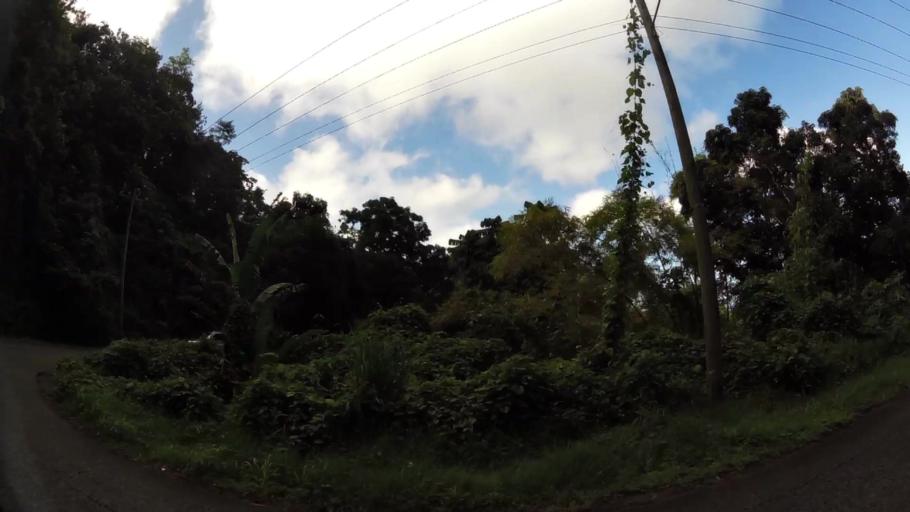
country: LC
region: Anse-la-Raye
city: Canaries
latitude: 13.9150
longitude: -61.0467
